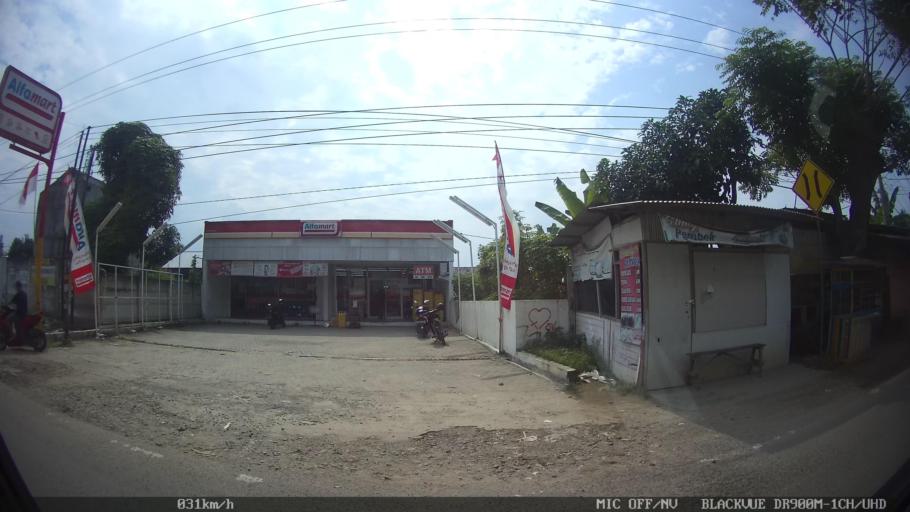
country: ID
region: Lampung
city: Bandarlampung
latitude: -5.4632
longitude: 105.2434
